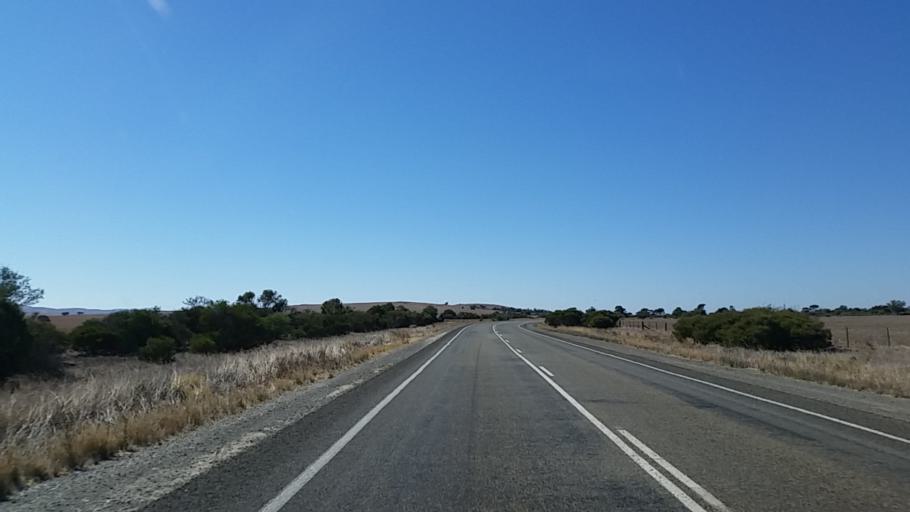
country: AU
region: South Australia
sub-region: Peterborough
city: Peterborough
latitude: -33.2352
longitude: 138.8778
